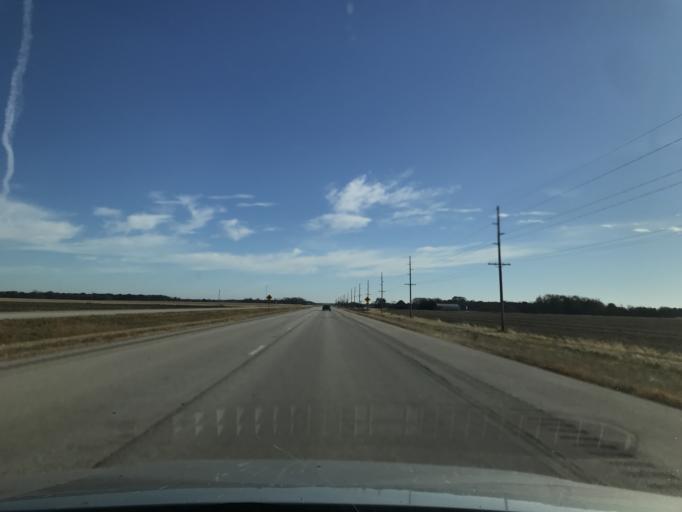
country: US
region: Illinois
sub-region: Hancock County
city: Carthage
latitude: 40.4152
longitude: -91.0586
